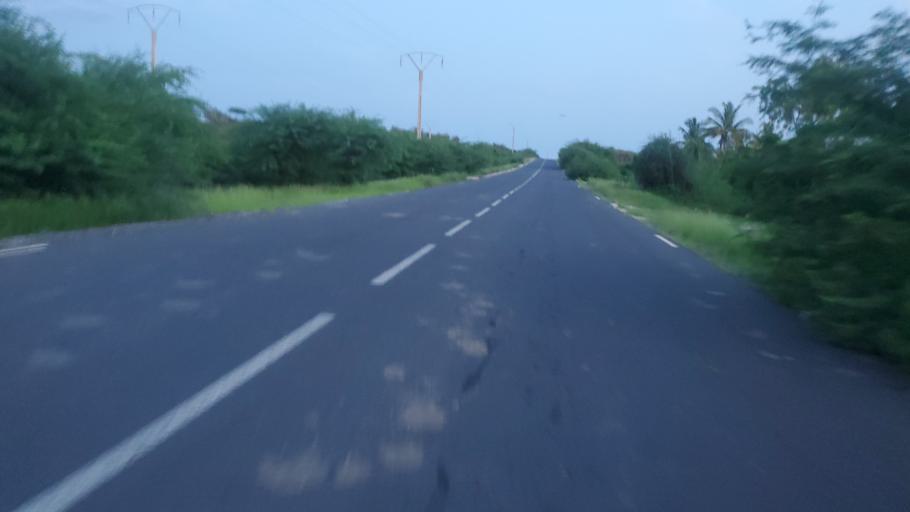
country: SN
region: Saint-Louis
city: Saint-Louis
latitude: 16.0790
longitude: -16.3910
